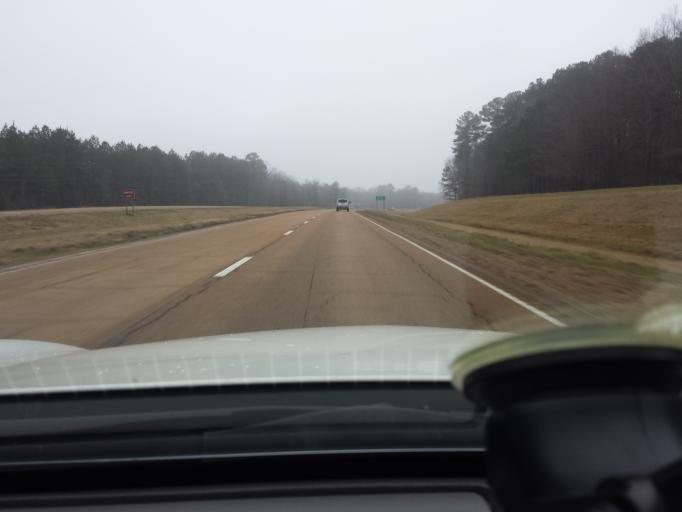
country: US
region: Mississippi
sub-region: Rankin County
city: Brandon
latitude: 32.4187
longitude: -89.9399
